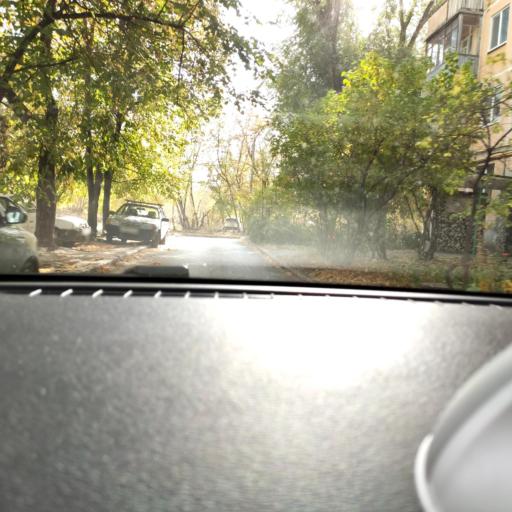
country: RU
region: Samara
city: Samara
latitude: 53.2374
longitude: 50.2367
